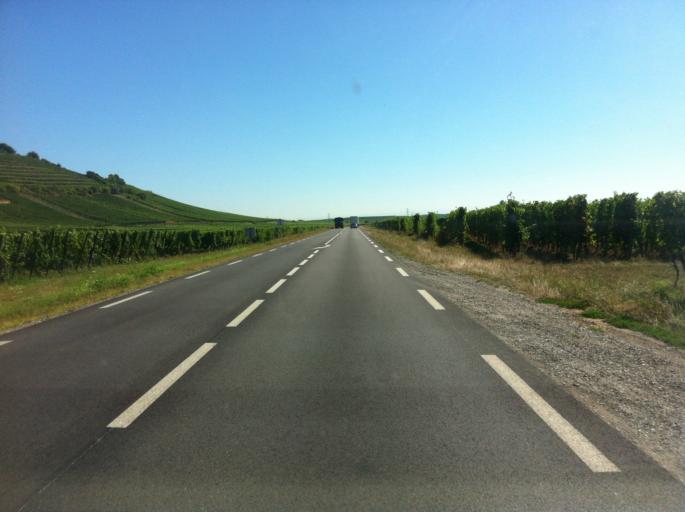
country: FR
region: Alsace
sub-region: Departement du Haut-Rhin
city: Sigolsheim
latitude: 48.1330
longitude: 7.3080
